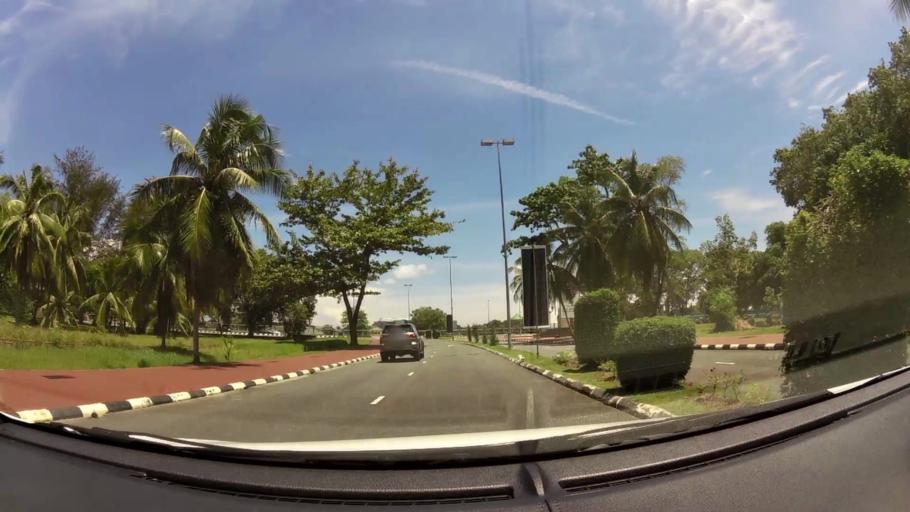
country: BN
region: Brunei and Muara
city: Bandar Seri Begawan
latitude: 4.9285
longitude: 114.9401
